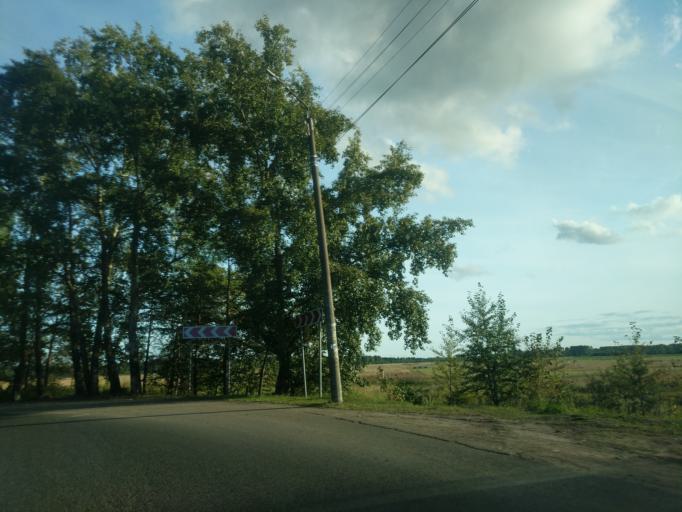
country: RU
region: Kirov
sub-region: Kirovo-Chepetskiy Rayon
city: Kirov
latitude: 58.6150
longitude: 49.7678
